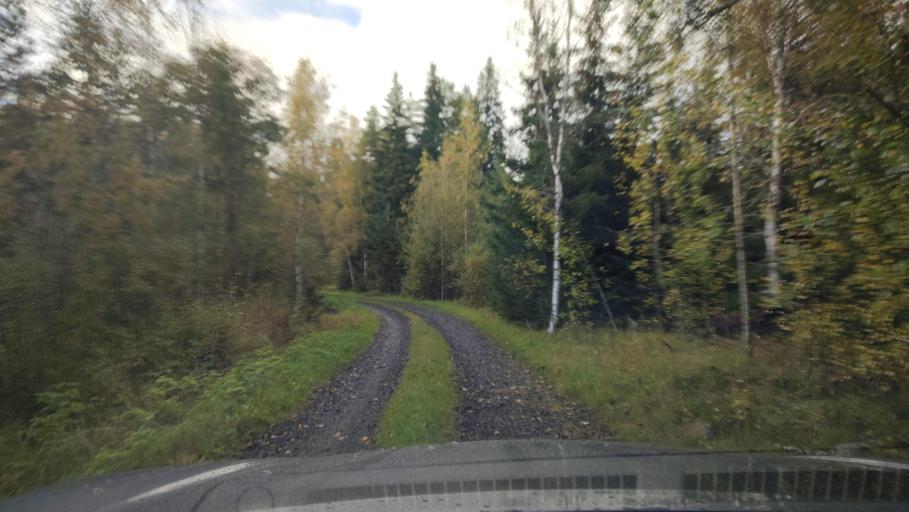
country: FI
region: Ostrobothnia
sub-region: Sydosterbotten
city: Kristinestad
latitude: 62.3048
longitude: 21.5040
